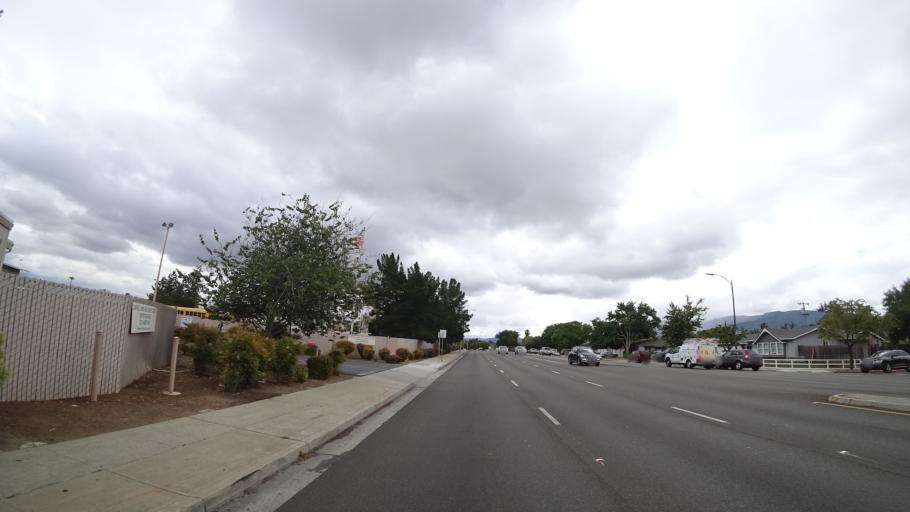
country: US
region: California
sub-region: Santa Clara County
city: Cambrian Park
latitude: 37.2645
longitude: -121.9388
